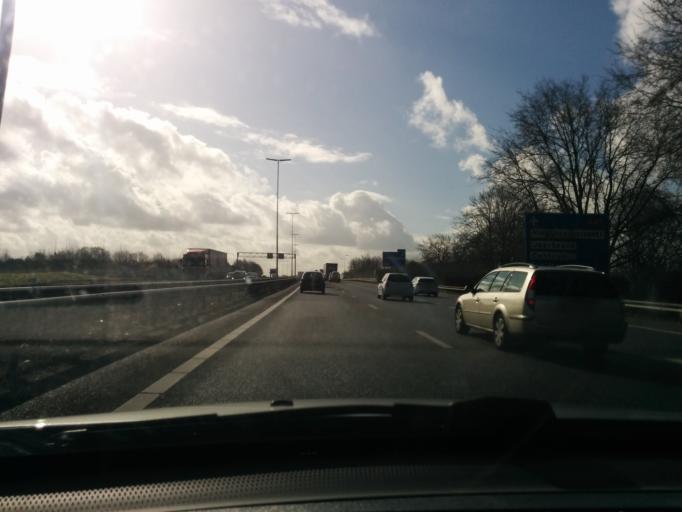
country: NL
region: Utrecht
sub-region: Gemeente De Bilt
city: De Bilt
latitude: 52.1272
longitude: 5.1486
